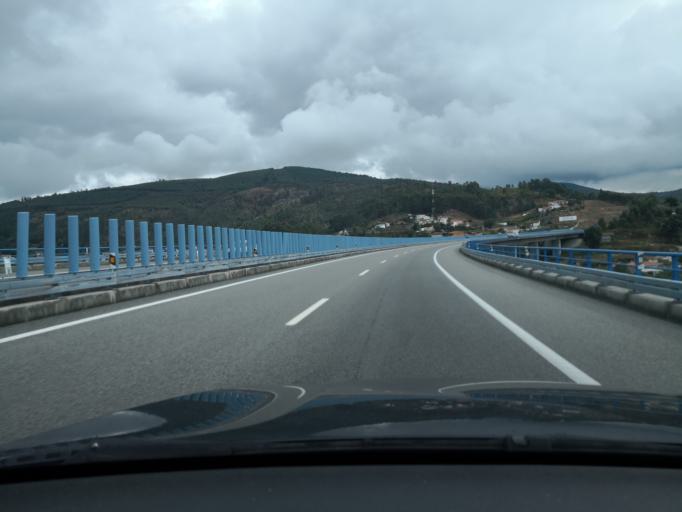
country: PT
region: Porto
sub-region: Pacos de Ferreira
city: Freamunde
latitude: 41.2942
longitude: -8.3093
